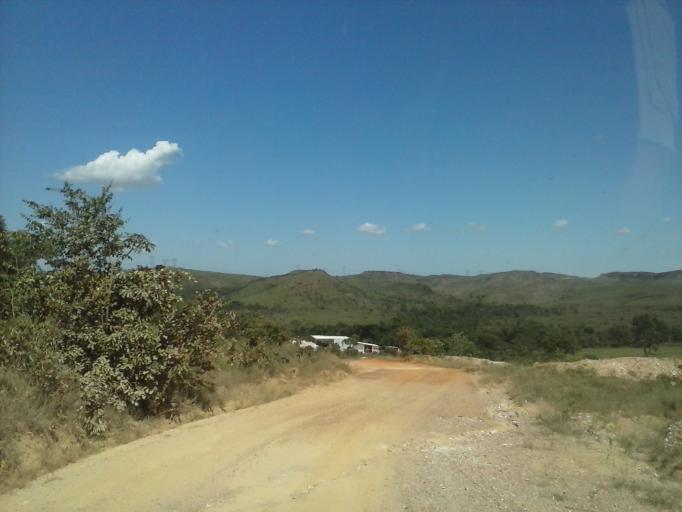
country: BR
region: Federal District
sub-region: Brasilia
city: Brasilia
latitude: -15.8871
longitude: -48.1938
